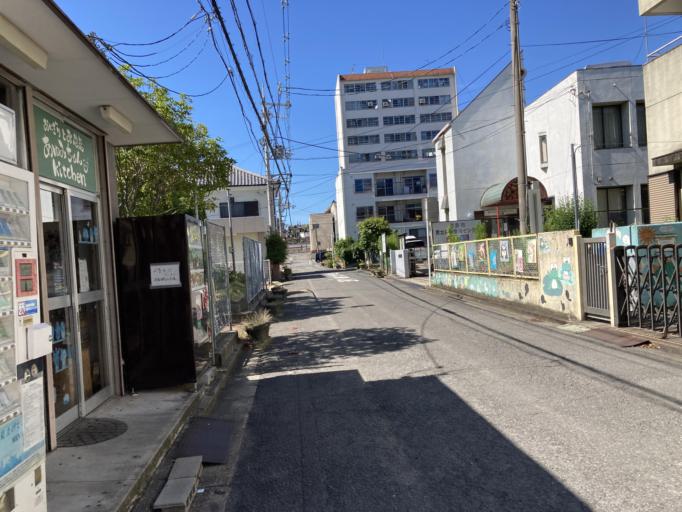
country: JP
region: Nara
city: Nara-shi
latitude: 34.6830
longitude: 135.8223
